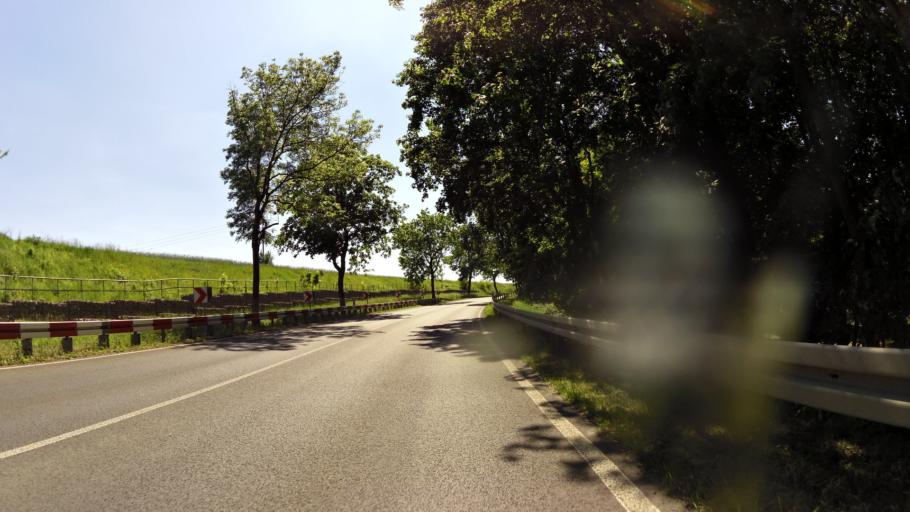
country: DE
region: Brandenburg
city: Lebus
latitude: 52.4067
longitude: 14.5238
